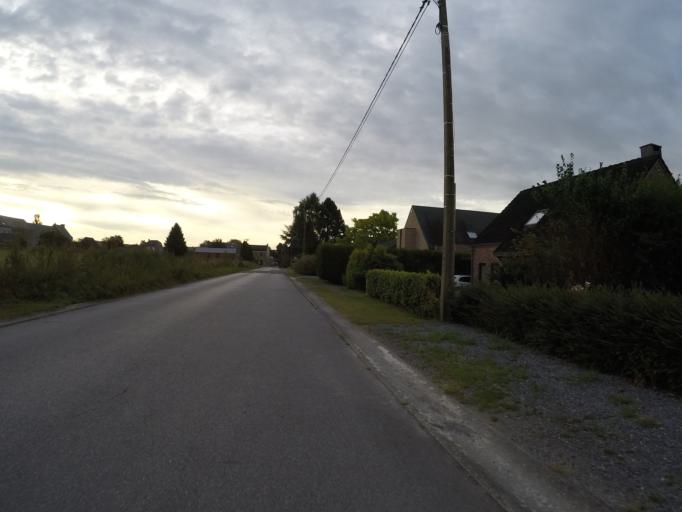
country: BE
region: Wallonia
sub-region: Province de Namur
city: Assesse
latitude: 50.3354
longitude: 5.0602
